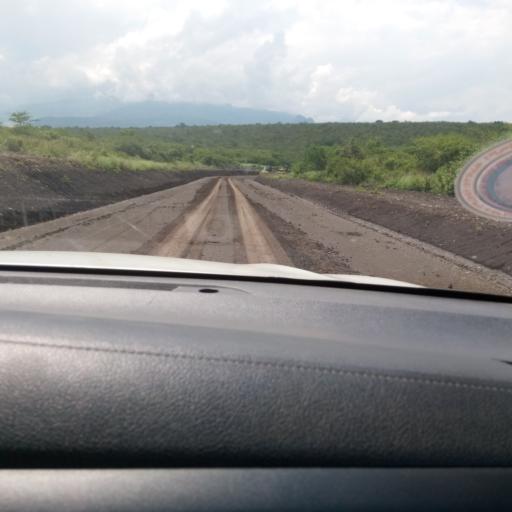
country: ET
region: Southern Nations, Nationalities, and People's Region
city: Arba Minch'
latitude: 6.3619
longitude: 37.2967
